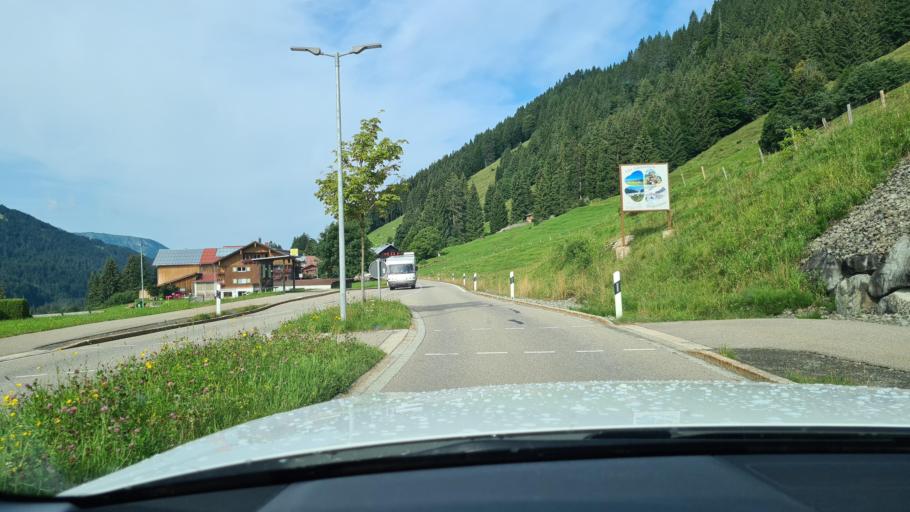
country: DE
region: Bavaria
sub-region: Swabia
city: Balderschwang
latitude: 47.4606
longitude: 10.0779
